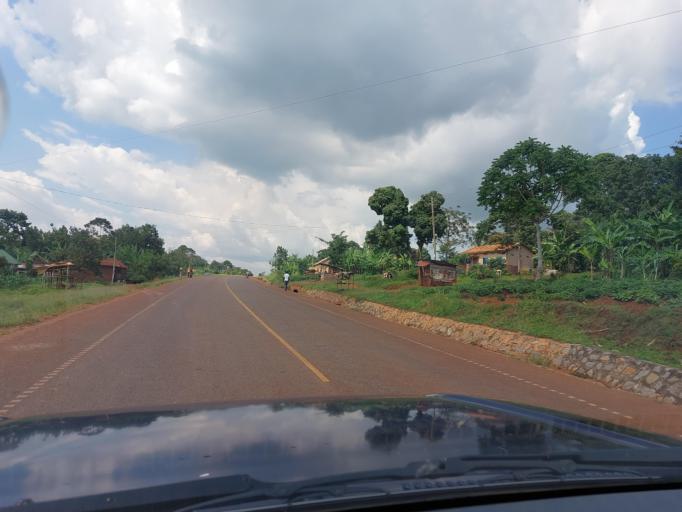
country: UG
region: Central Region
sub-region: Buikwe District
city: Buikwe
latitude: 0.3275
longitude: 33.1157
